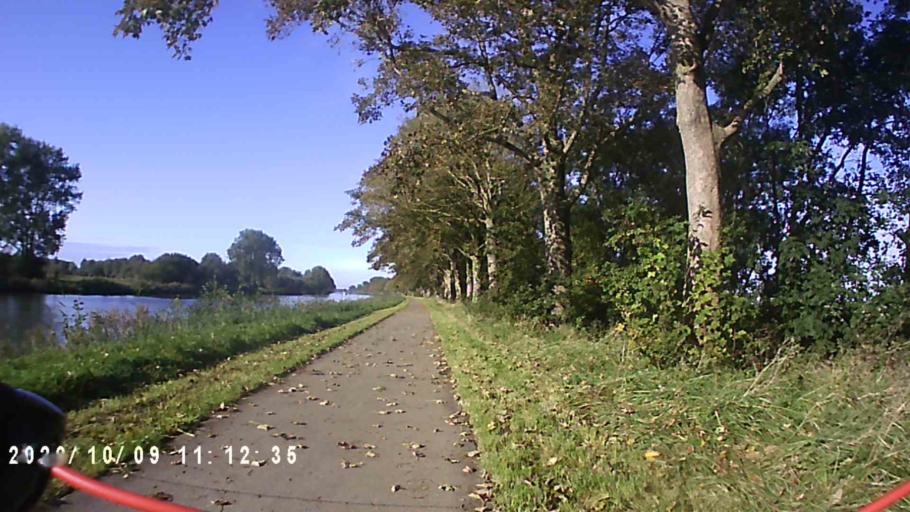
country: NL
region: Groningen
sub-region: Gemeente Zuidhorn
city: Aduard
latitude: 53.2614
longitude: 6.4473
